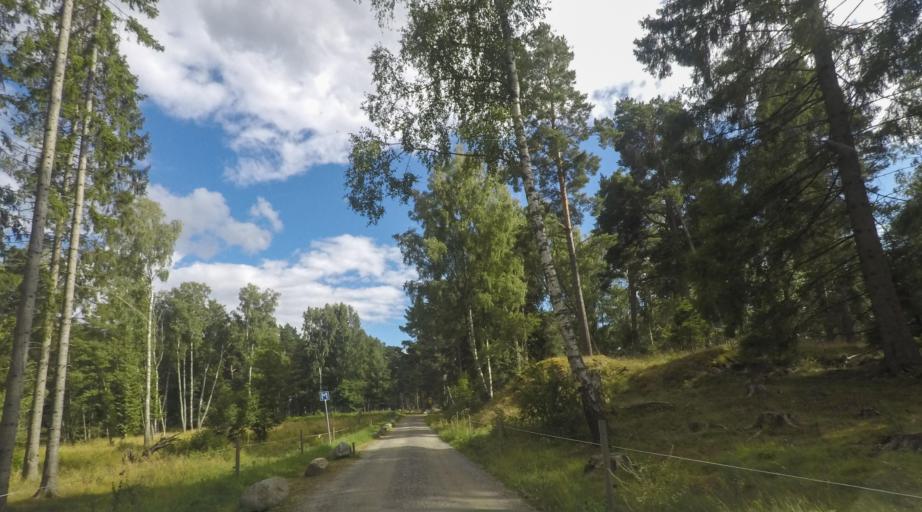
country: SE
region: Stockholm
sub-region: Sodertalje Kommun
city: Pershagen
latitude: 59.1046
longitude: 17.6790
